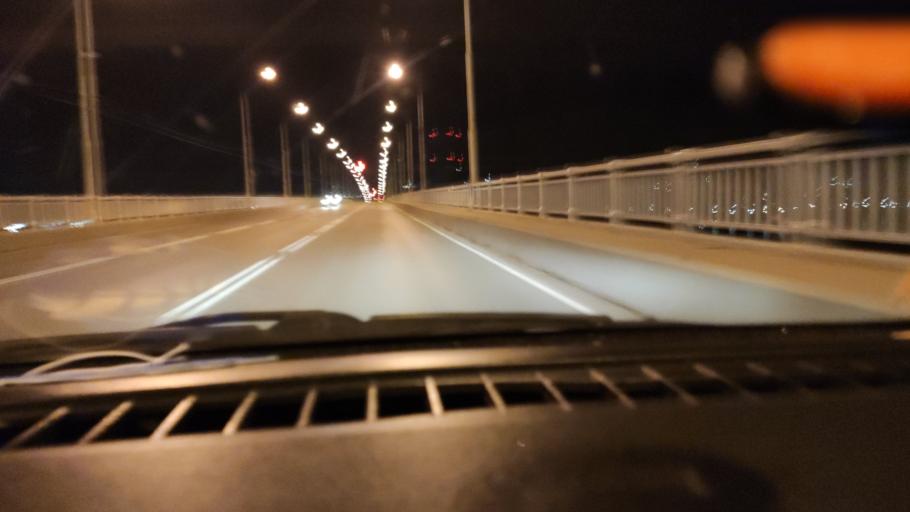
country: RU
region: Saratov
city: Engel's
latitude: 51.5210
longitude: 46.0681
